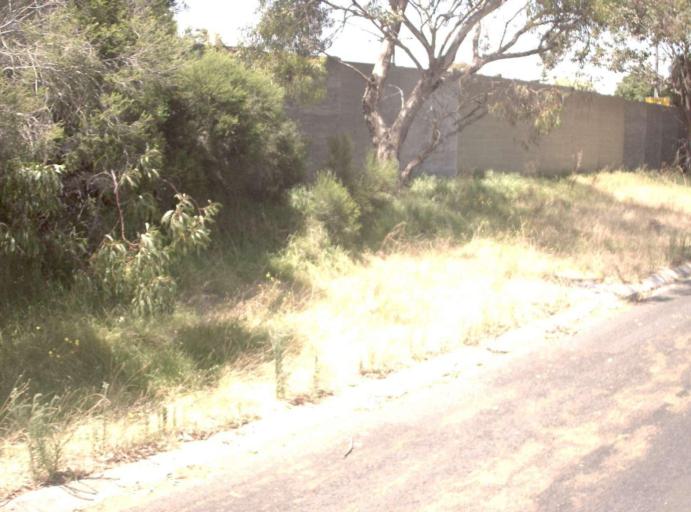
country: AU
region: Victoria
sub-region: Frankston
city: Seaford
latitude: -38.1049
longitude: 145.1402
